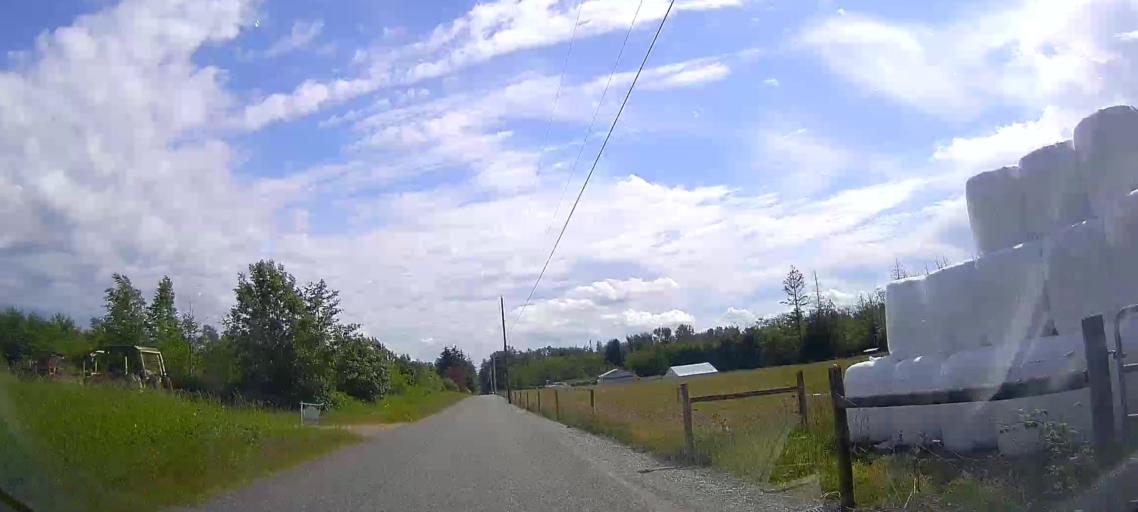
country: US
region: Washington
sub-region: Skagit County
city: Burlington
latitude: 48.5478
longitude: -122.3621
